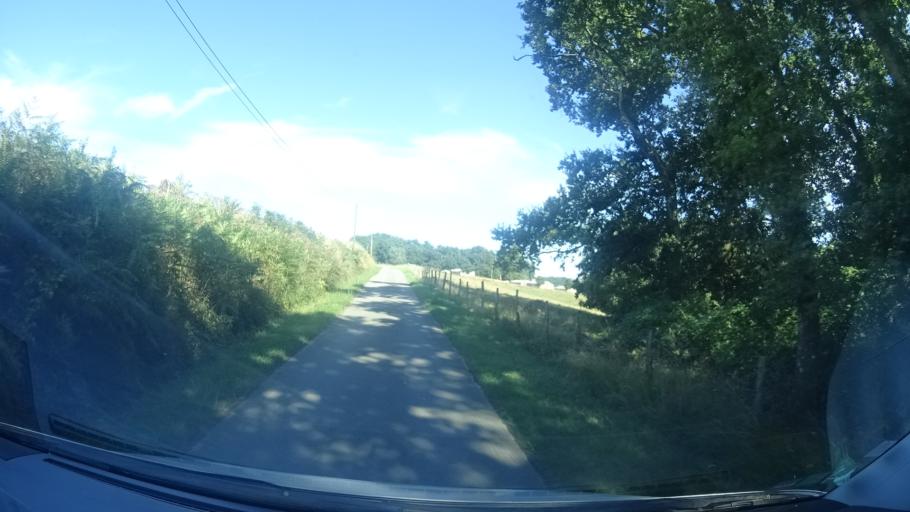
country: FR
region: Aquitaine
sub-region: Departement des Pyrenees-Atlantiques
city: Orthez
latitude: 43.5070
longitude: -0.7008
